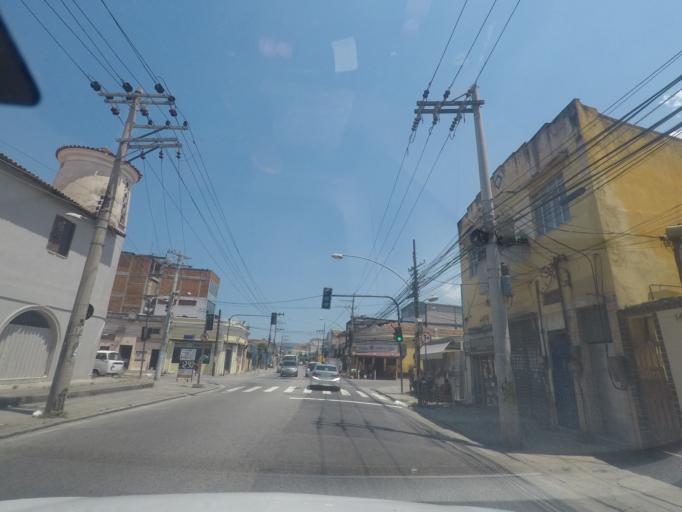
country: BR
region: Rio de Janeiro
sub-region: Duque De Caxias
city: Duque de Caxias
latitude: -22.8471
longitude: -43.2675
